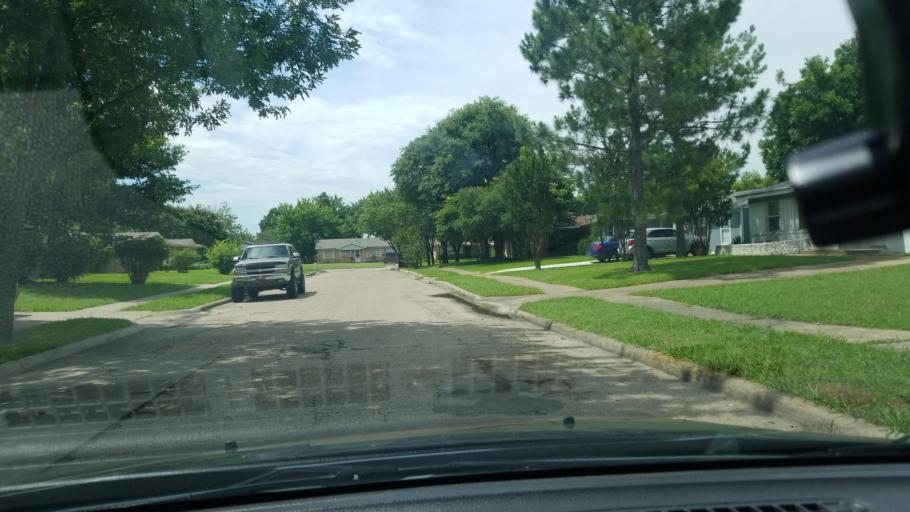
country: US
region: Texas
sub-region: Dallas County
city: Mesquite
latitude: 32.7544
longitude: -96.5808
